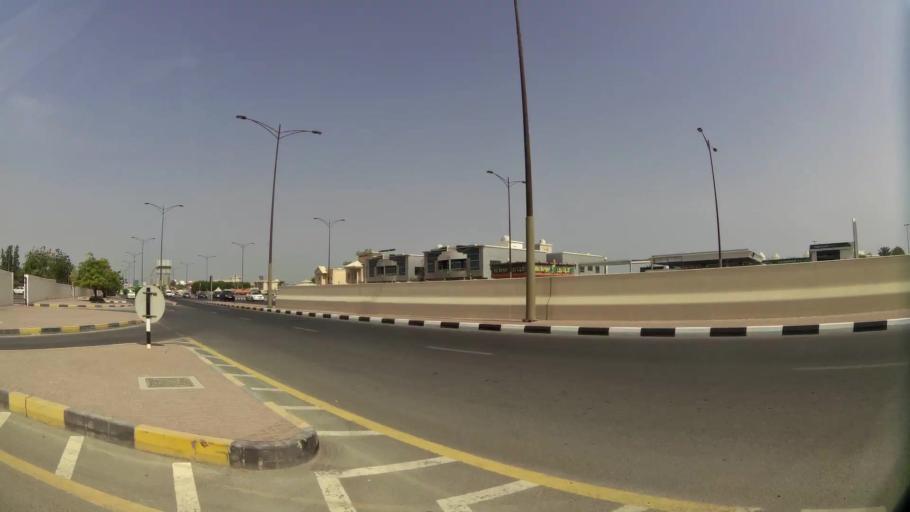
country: AE
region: Ash Shariqah
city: Sharjah
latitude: 25.3552
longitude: 55.4246
